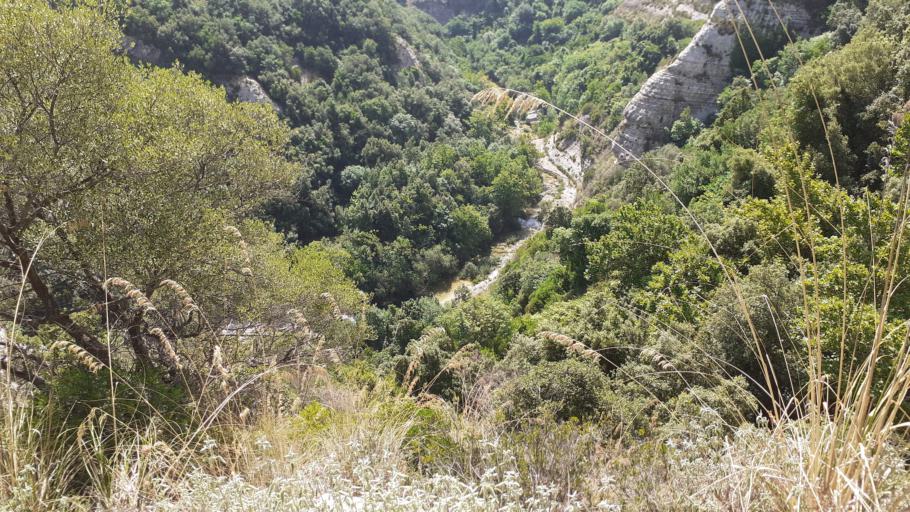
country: IT
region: Sicily
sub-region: Provincia di Siracusa
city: Canicattini Bagni
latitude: 36.9736
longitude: 15.0857
